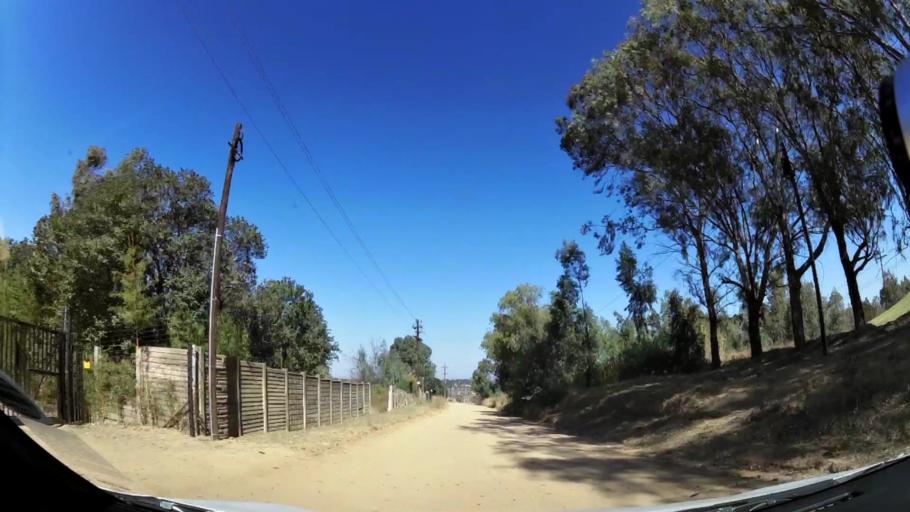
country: ZA
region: Gauteng
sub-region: City of Johannesburg Metropolitan Municipality
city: Midrand
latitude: -25.9397
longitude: 28.0860
